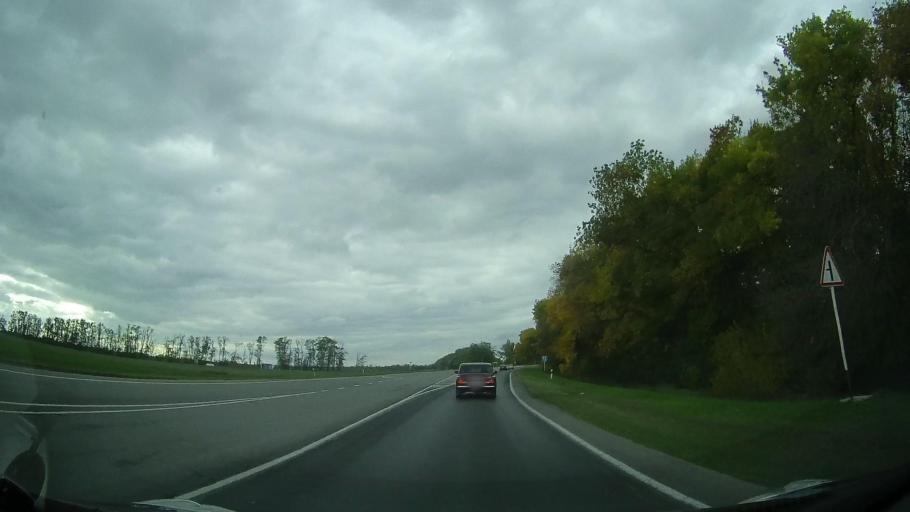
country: RU
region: Rostov
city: Yegorlykskaya
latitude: 46.5369
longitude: 40.7841
